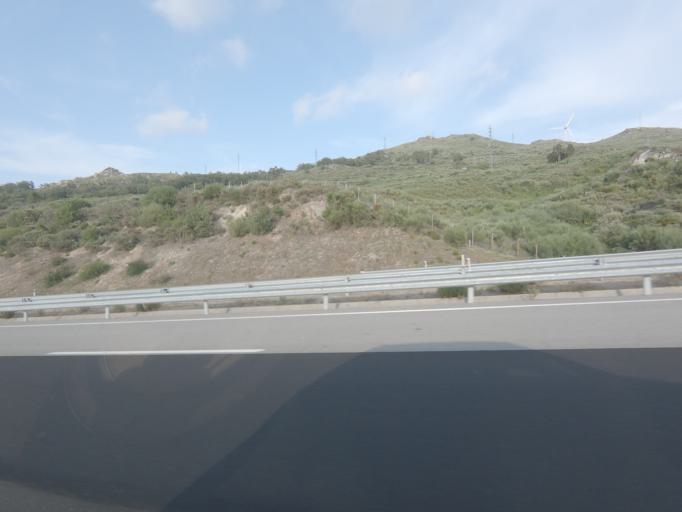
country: PT
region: Vila Real
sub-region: Vila Pouca de Aguiar
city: Vila Pouca de Aguiar
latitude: 41.4695
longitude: -7.6448
